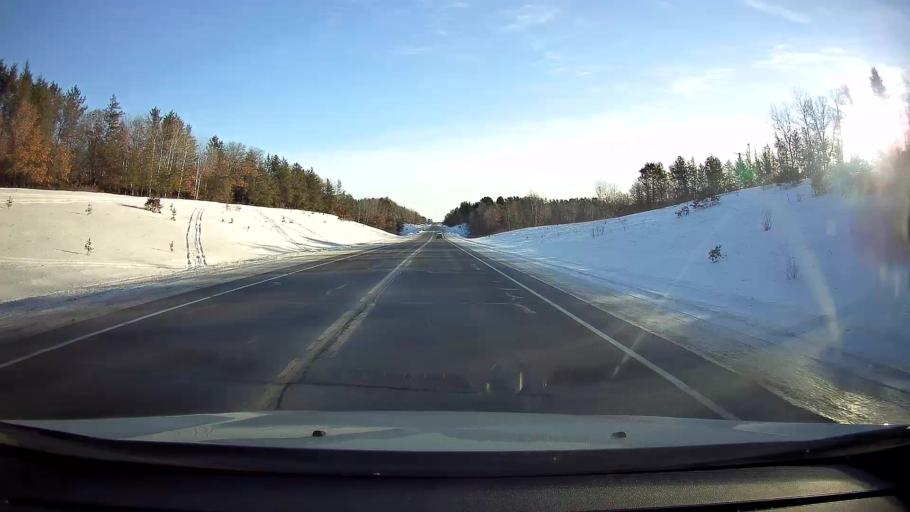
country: US
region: Wisconsin
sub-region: Washburn County
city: Spooner
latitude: 45.9104
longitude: -91.7852
